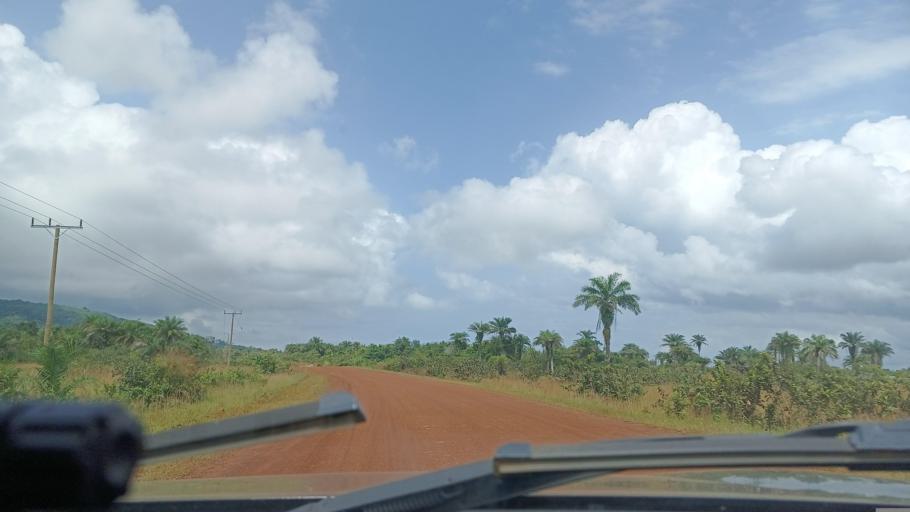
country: LR
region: Grand Cape Mount
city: Robertsport
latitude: 6.7479
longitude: -11.3415
